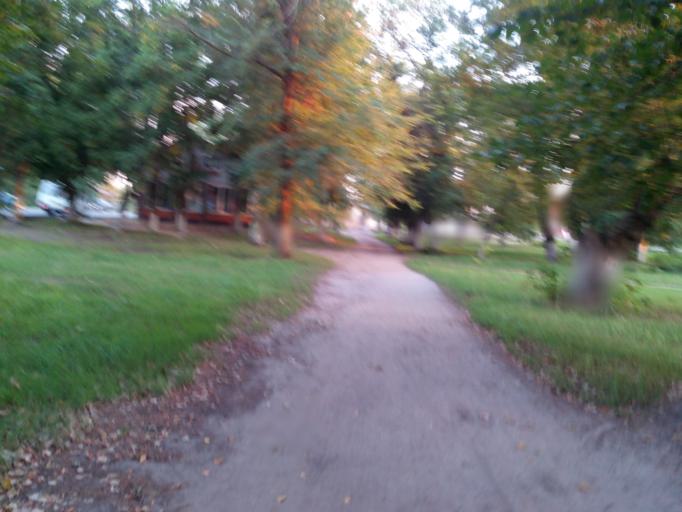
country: RU
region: Voronezj
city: Borisoglebsk
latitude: 51.3582
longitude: 42.0762
